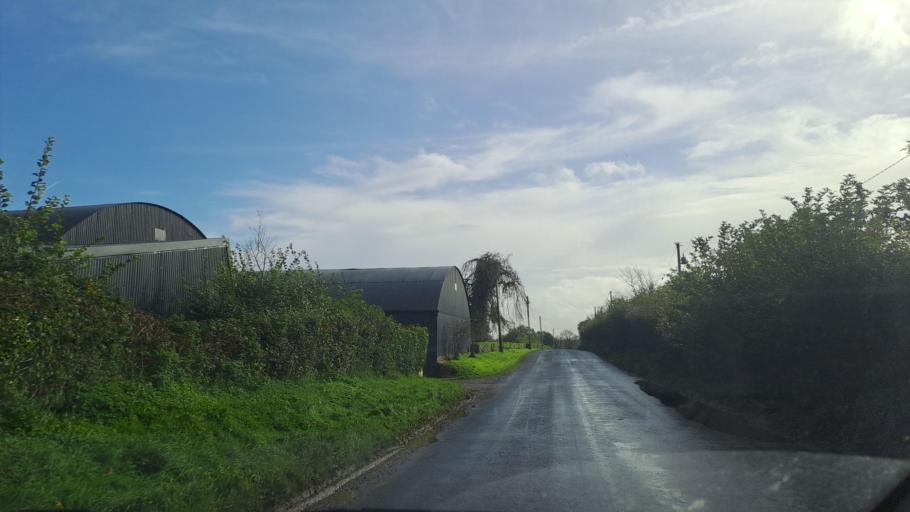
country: IE
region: Ulster
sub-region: County Monaghan
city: Carrickmacross
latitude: 53.8692
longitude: -6.6632
